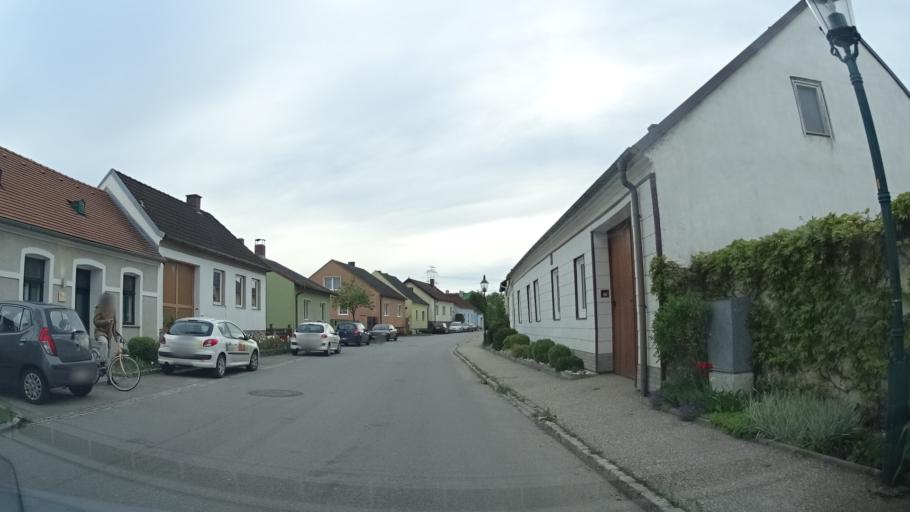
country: AT
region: Lower Austria
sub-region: Politischer Bezirk Korneuburg
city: Harmannsdorf
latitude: 48.3801
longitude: 16.3519
